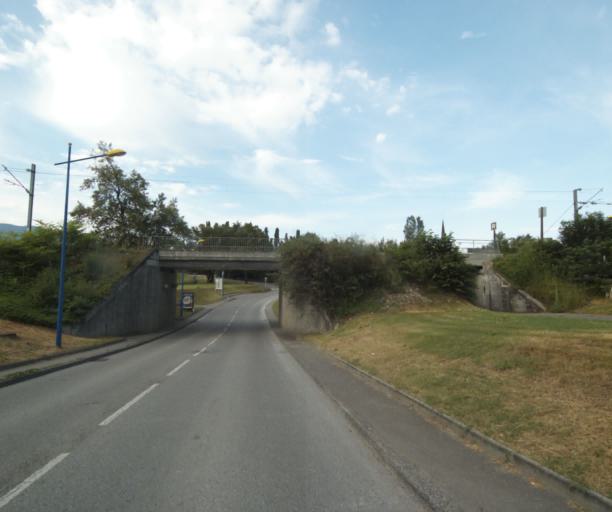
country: FR
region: Rhone-Alpes
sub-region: Departement de la Haute-Savoie
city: Marin
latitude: 46.3842
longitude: 6.5071
